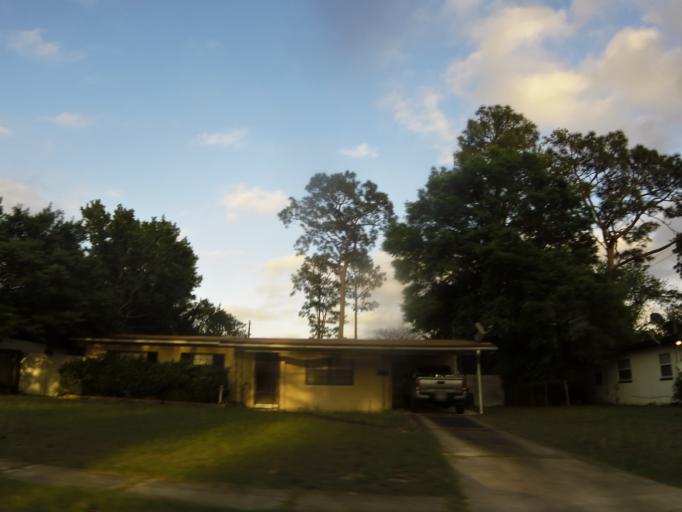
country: US
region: Florida
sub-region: Duval County
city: Jacksonville
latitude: 30.4442
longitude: -81.6297
